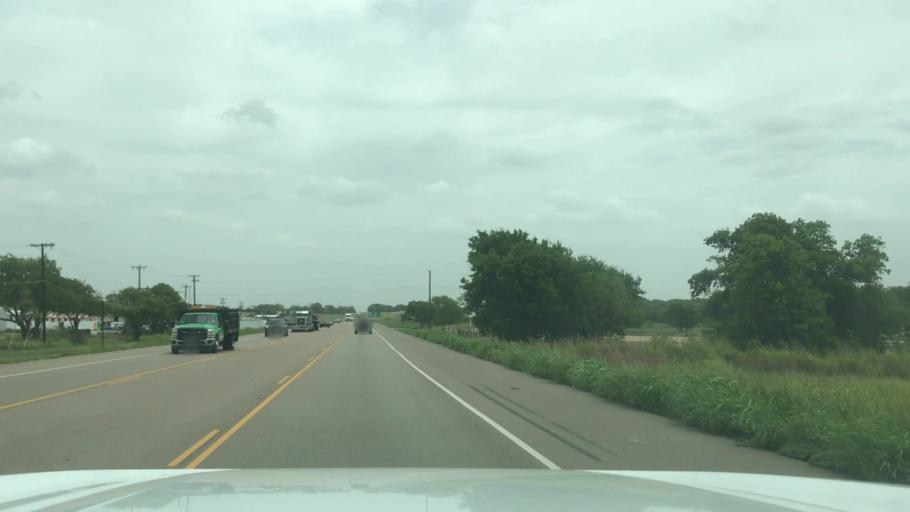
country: US
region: Texas
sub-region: McLennan County
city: Woodway
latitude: 31.5787
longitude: -97.2988
